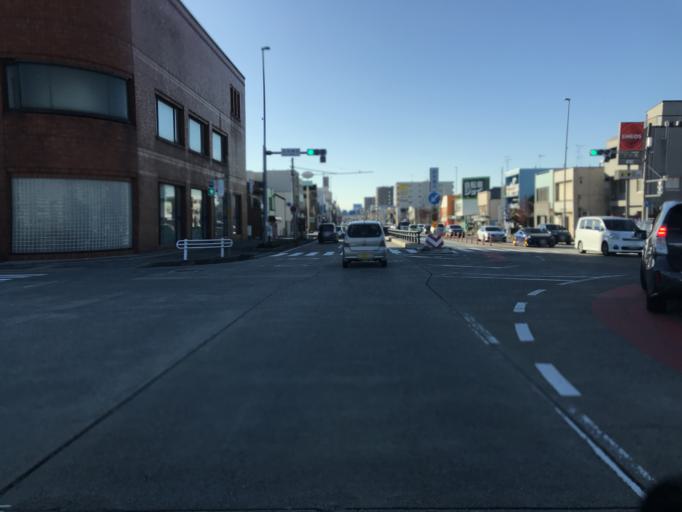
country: JP
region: Aichi
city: Nagoya-shi
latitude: 35.1252
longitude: 136.8759
